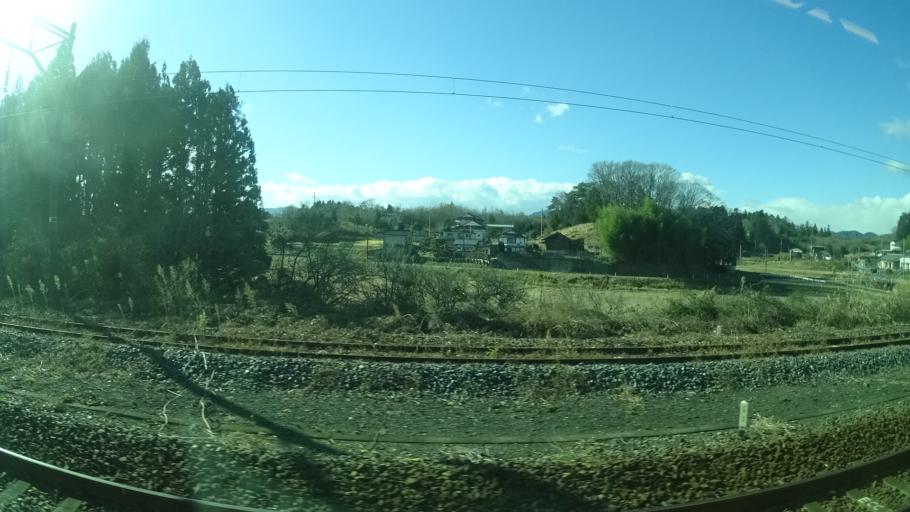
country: JP
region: Miyagi
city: Marumori
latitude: 37.7542
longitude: 140.9363
